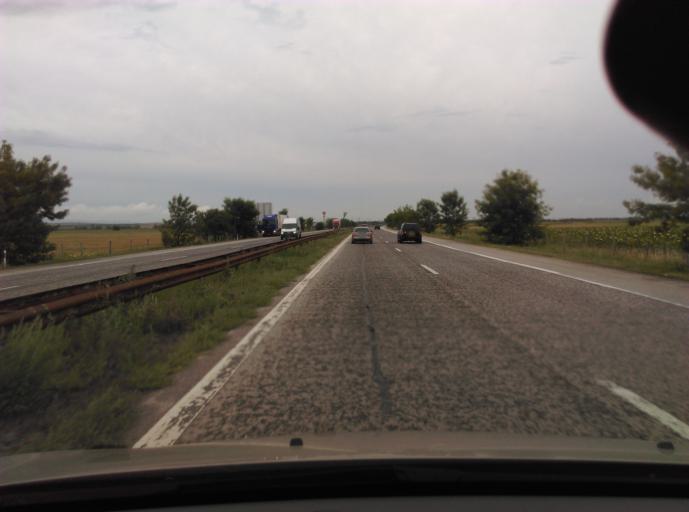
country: BG
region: Plovdiv
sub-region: Obshtina Rakovski
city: Rakovski
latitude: 42.2186
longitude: 25.0339
